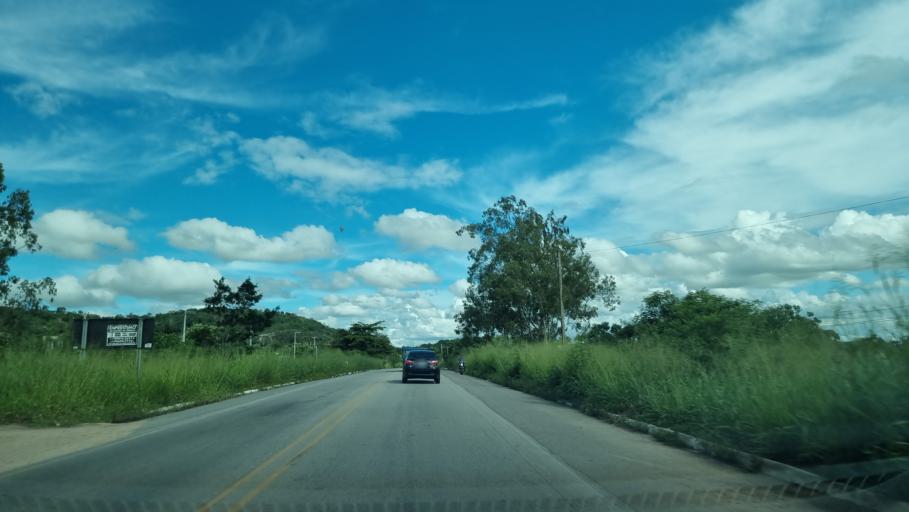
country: BR
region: Pernambuco
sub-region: Caruaru
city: Caruaru
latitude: -8.3746
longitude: -35.9838
